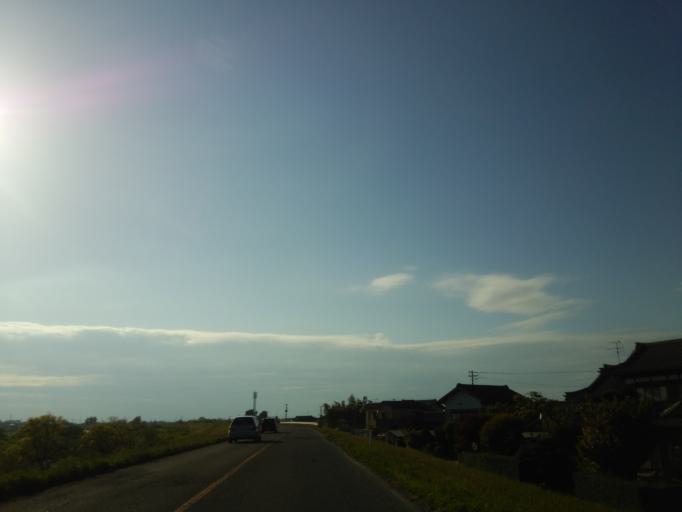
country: JP
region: Niigata
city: Gosen
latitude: 37.7809
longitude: 139.1944
